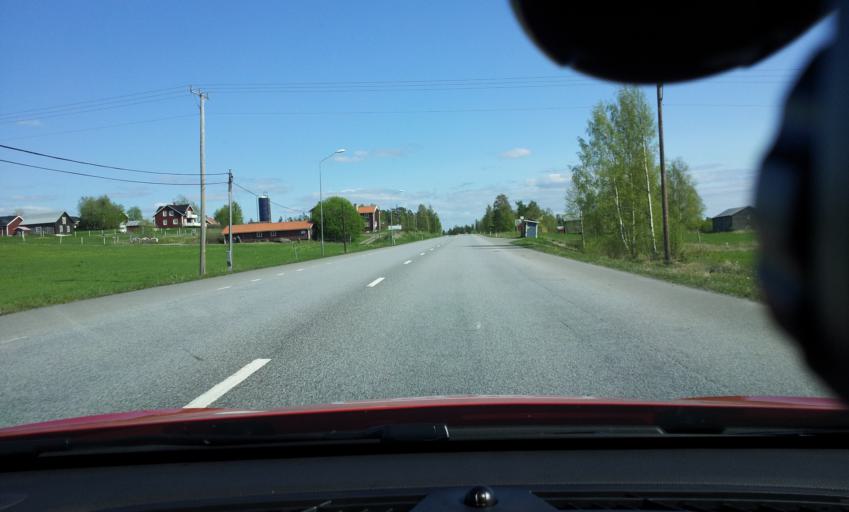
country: SE
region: Jaemtland
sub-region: Krokoms Kommun
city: Krokom
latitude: 63.3177
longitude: 14.0863
